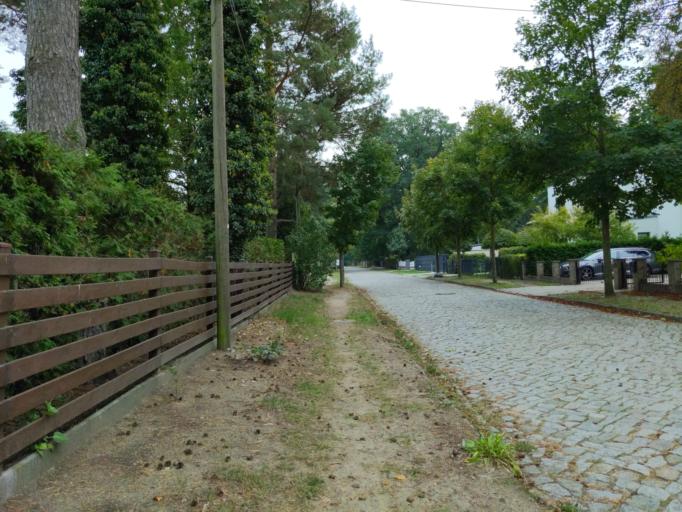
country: DE
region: Brandenburg
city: Michendorf
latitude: 52.3341
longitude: 13.0484
